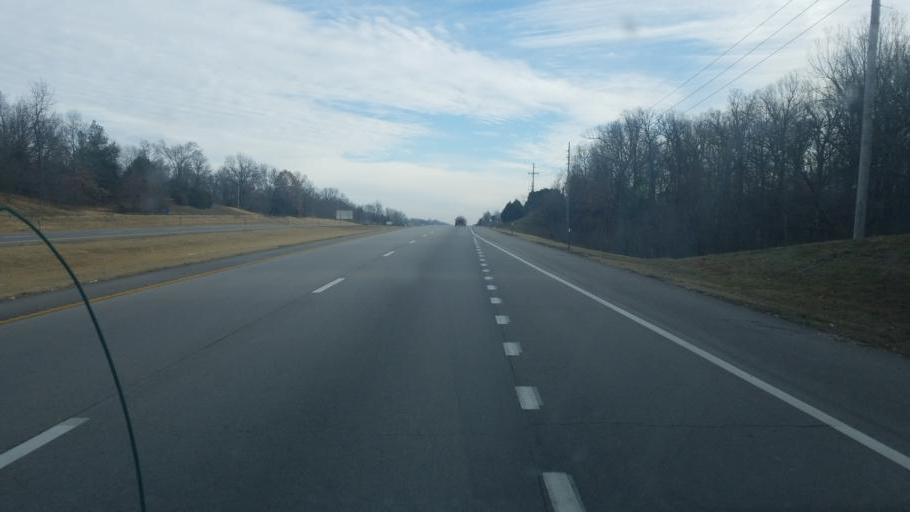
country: US
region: Missouri
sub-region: Stoddard County
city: Dexter
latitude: 36.8105
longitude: -89.9648
